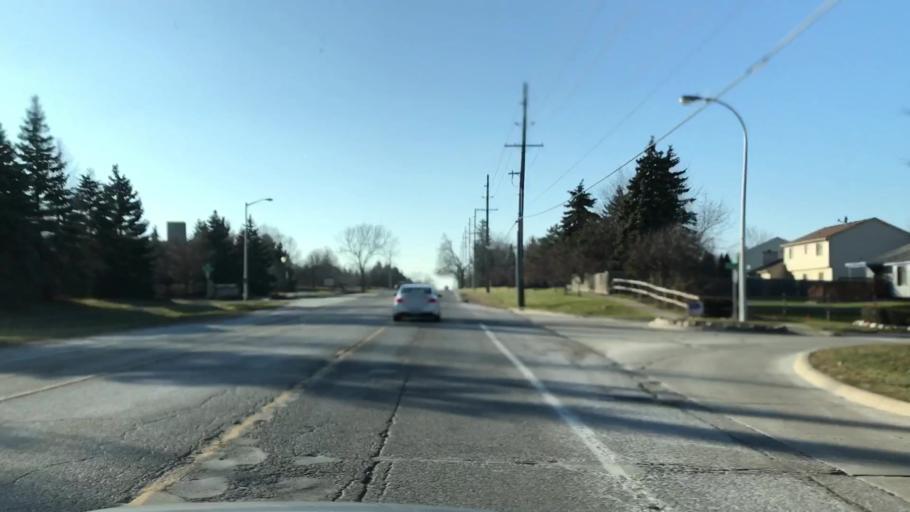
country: US
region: Michigan
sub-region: Oakland County
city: Novi
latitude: 42.4654
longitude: -83.5002
